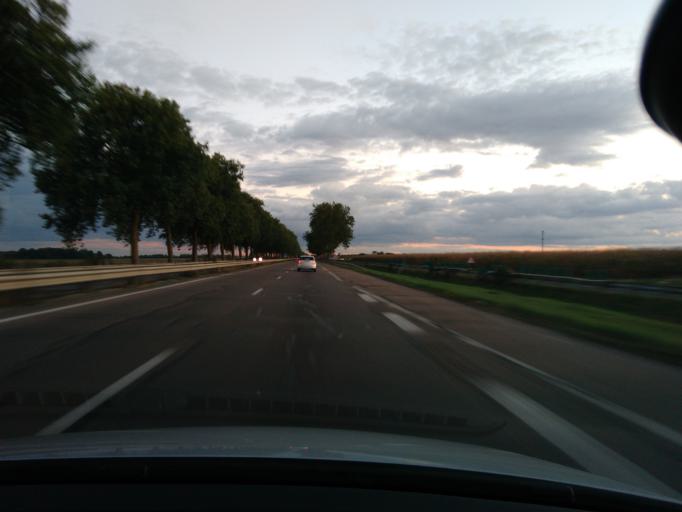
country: FR
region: Ile-de-France
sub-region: Departement de Seine-et-Marne
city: Nanteuil-les-Meaux
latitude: 48.9244
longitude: 2.8804
